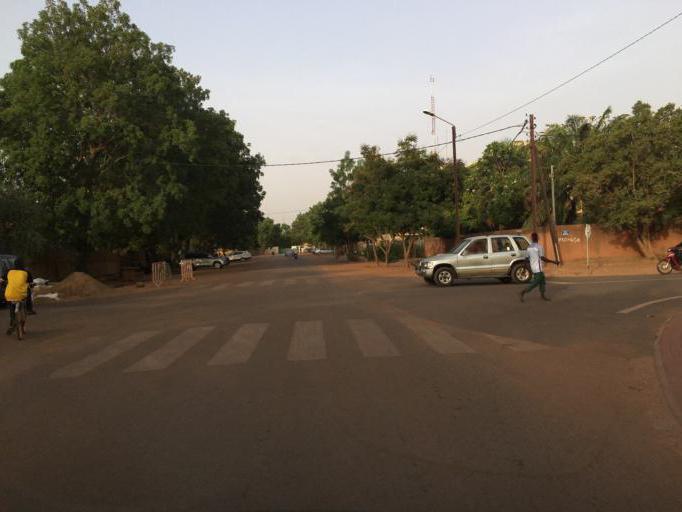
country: BF
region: Centre
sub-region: Kadiogo Province
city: Ouagadougou
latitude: 12.3705
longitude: -1.5125
